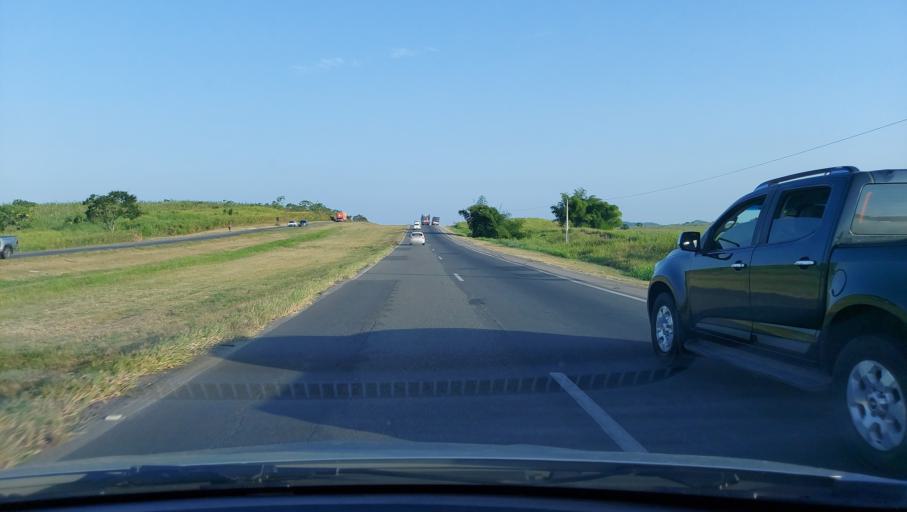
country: BR
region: Bahia
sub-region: Santo Amaro
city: Santo Amaro
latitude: -12.4884
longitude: -38.6591
